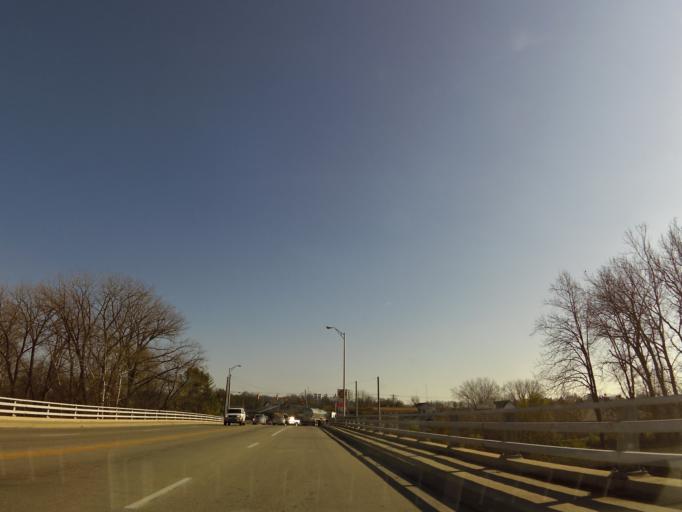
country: US
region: Indiana
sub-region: Fayette County
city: Connersville
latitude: 39.6392
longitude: -85.1308
